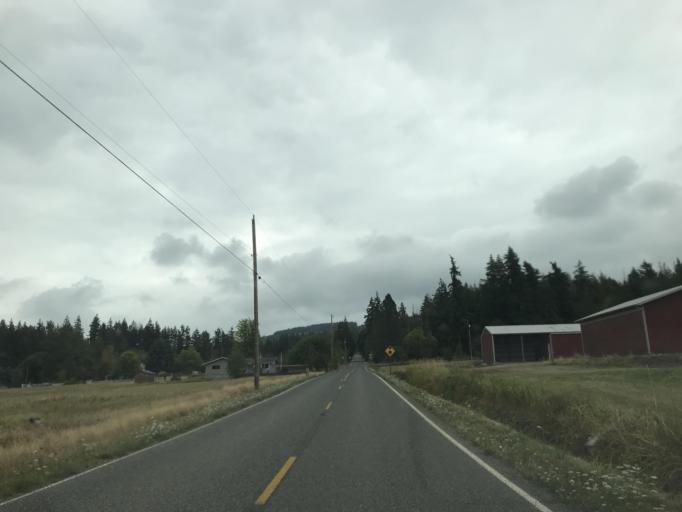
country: US
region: Washington
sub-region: Whatcom County
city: Sudden Valley
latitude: 48.8181
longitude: -122.3350
